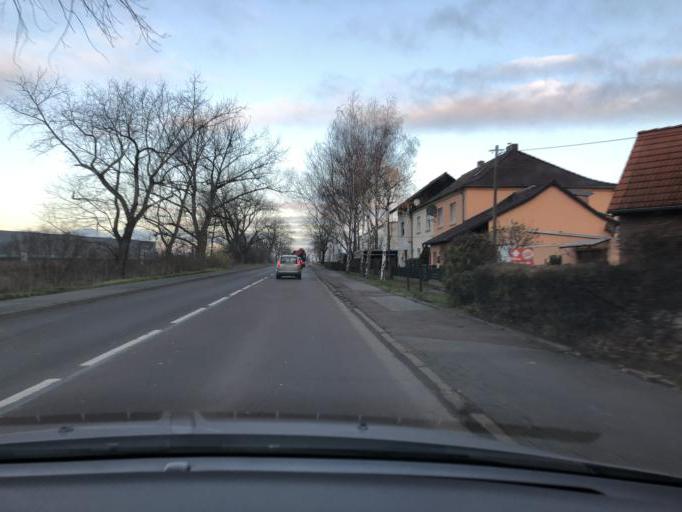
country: DE
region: Saxony-Anhalt
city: Dieskau
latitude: 51.4467
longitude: 12.0257
